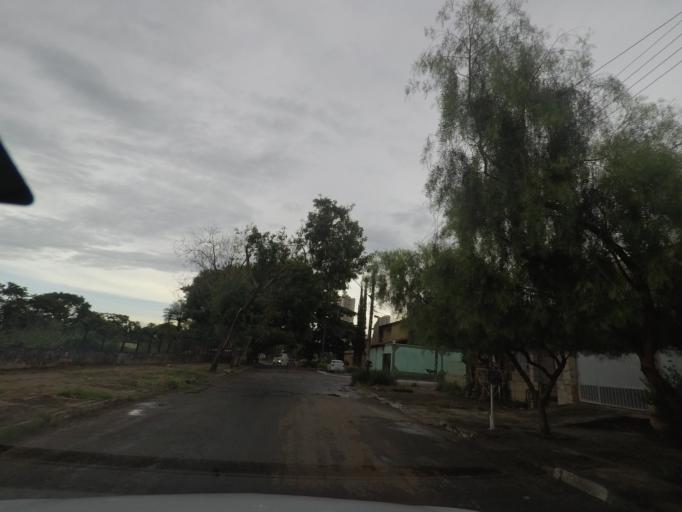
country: BR
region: Goias
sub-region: Goiania
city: Goiania
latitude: -16.7165
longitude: -49.2446
